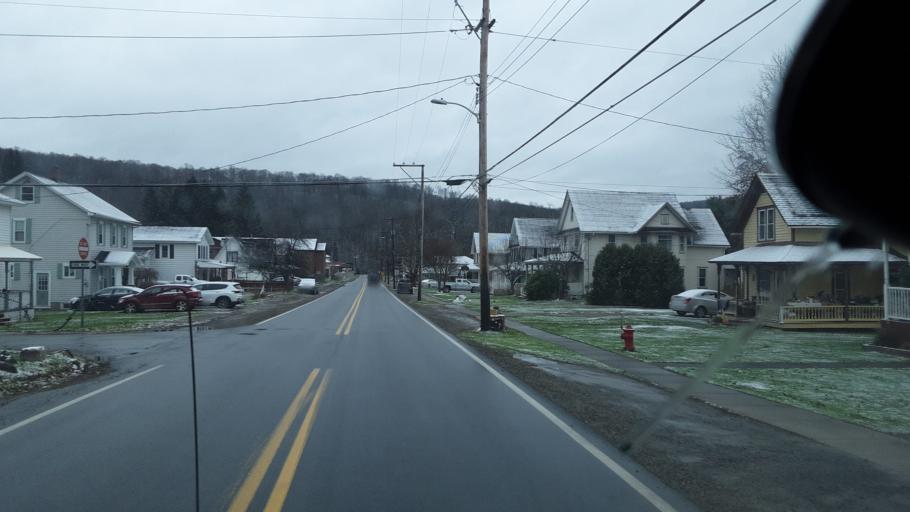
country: US
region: Pennsylvania
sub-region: Potter County
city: Shinglehouse
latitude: 41.9645
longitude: -78.1944
